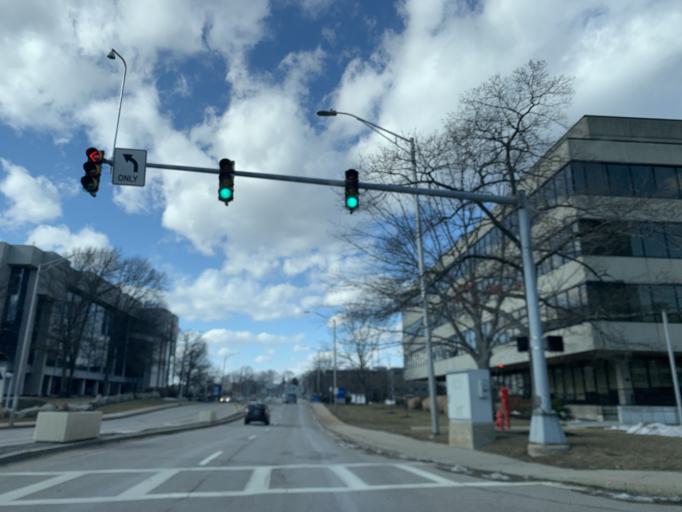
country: US
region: Massachusetts
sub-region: Norfolk County
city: Quincy
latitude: 42.2764
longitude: -71.0322
